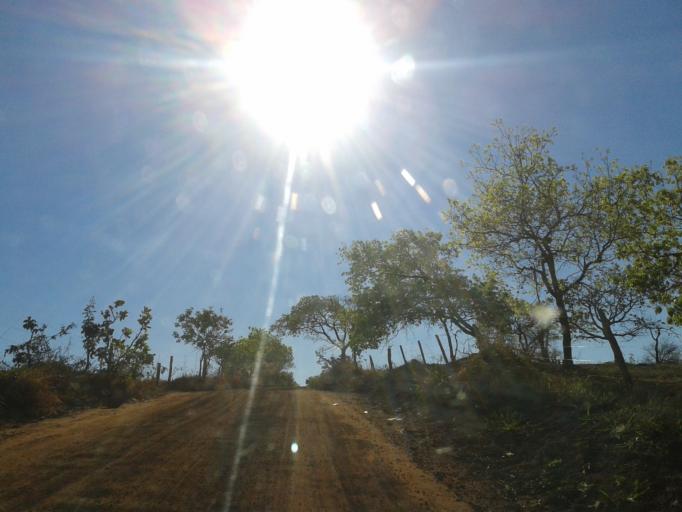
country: BR
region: Minas Gerais
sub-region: Ituiutaba
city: Ituiutaba
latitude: -19.0636
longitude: -49.3506
